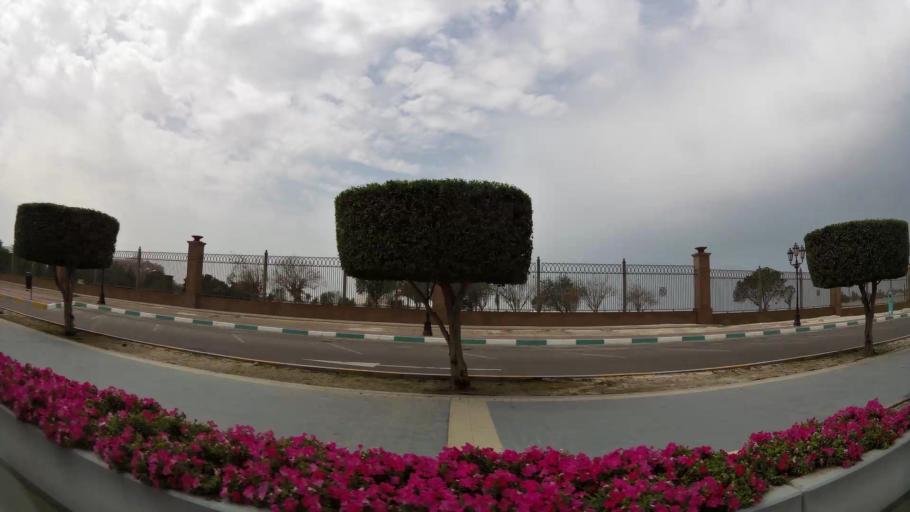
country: AE
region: Abu Dhabi
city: Abu Dhabi
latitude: 24.4679
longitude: 54.3225
